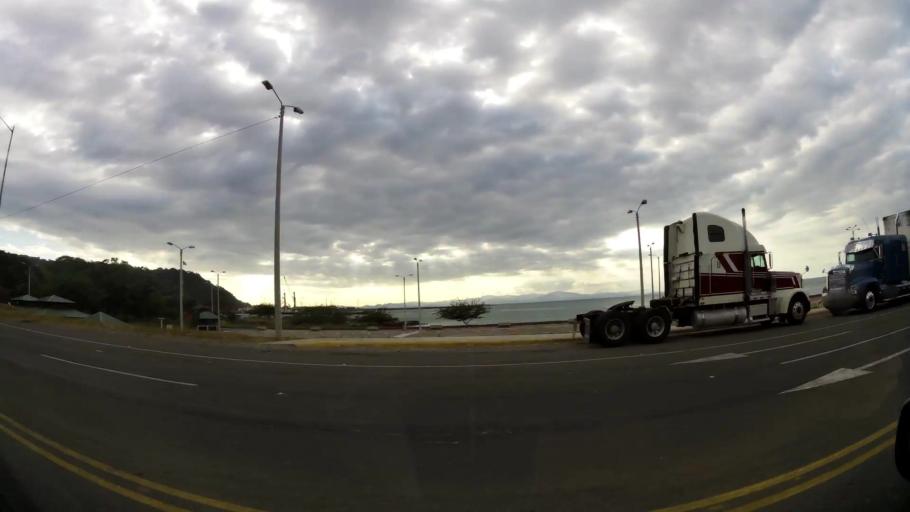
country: CR
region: Puntarenas
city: Esparza
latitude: 9.9182
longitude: -84.7122
